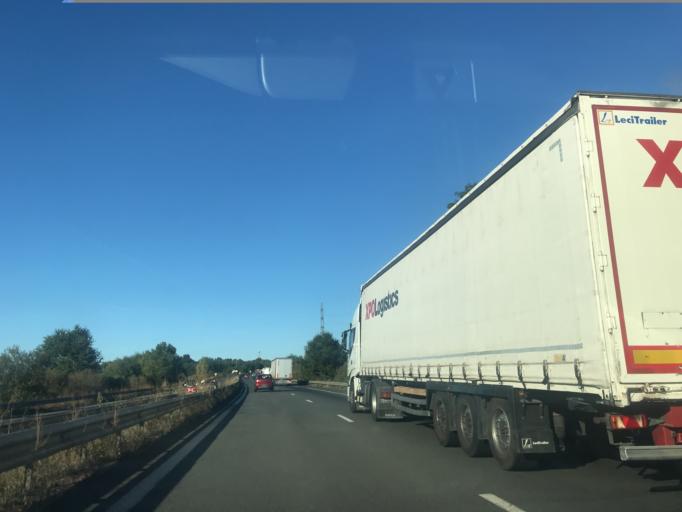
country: FR
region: Poitou-Charentes
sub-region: Departement de la Charente-Maritime
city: Montlieu-la-Garde
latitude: 45.2335
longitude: -0.2776
